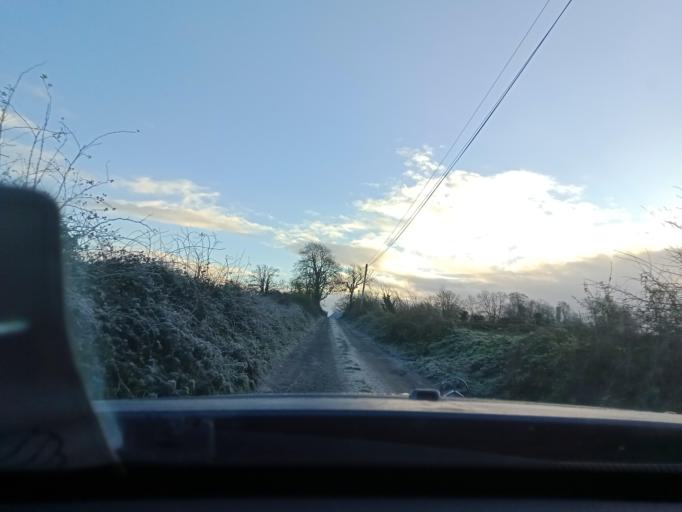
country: IE
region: Leinster
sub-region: County Carlow
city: Bagenalstown
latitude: 52.6389
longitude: -7.0057
